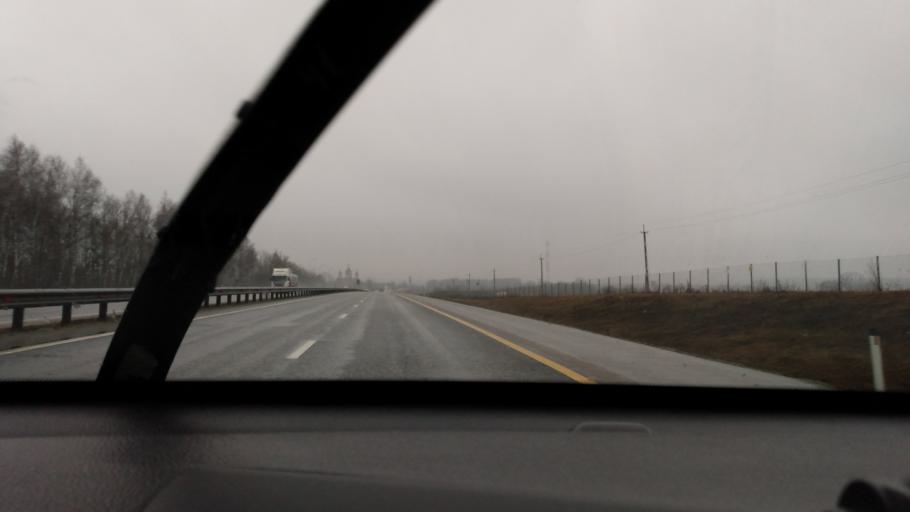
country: RU
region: Tula
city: Gritsovskiy
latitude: 54.2502
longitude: 38.1456
